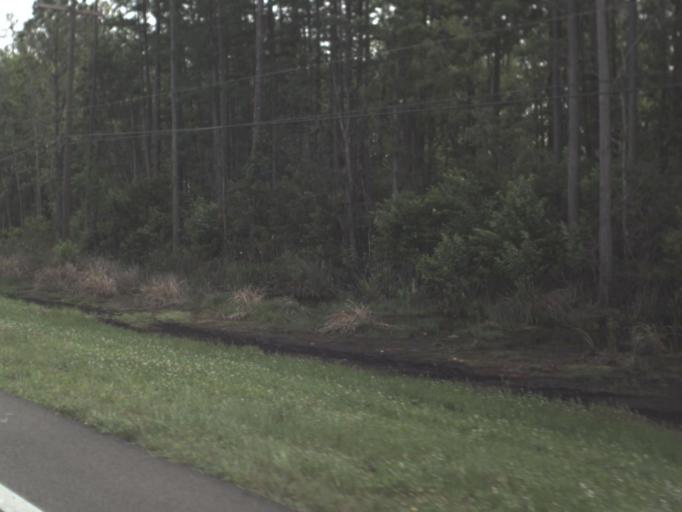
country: US
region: Florida
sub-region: Saint Johns County
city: Fruit Cove
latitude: 30.0999
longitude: -81.7056
